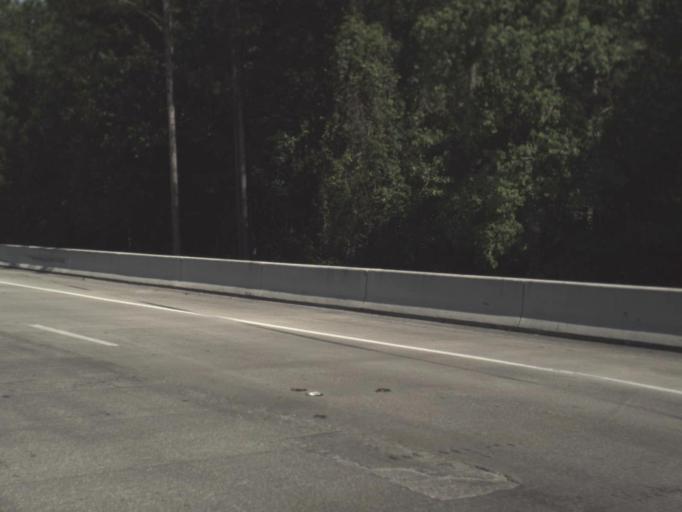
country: US
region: Florida
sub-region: Duval County
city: Jacksonville Beach
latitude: 30.2537
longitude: -81.5077
